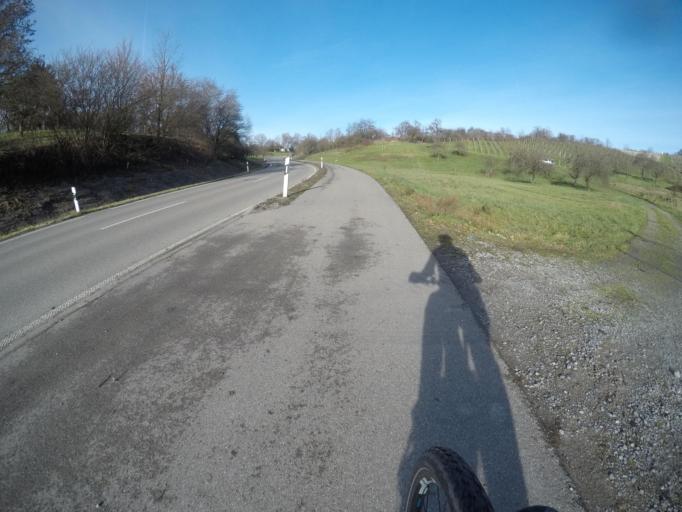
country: DE
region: Baden-Wuerttemberg
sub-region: Regierungsbezirk Stuttgart
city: Korb
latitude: 48.8494
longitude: 9.3566
